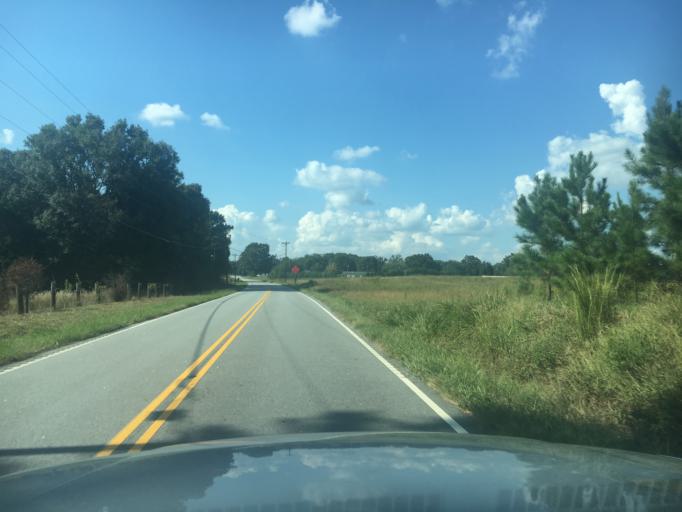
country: US
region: South Carolina
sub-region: Greenville County
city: Fountain Inn
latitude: 34.5914
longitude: -82.2236
